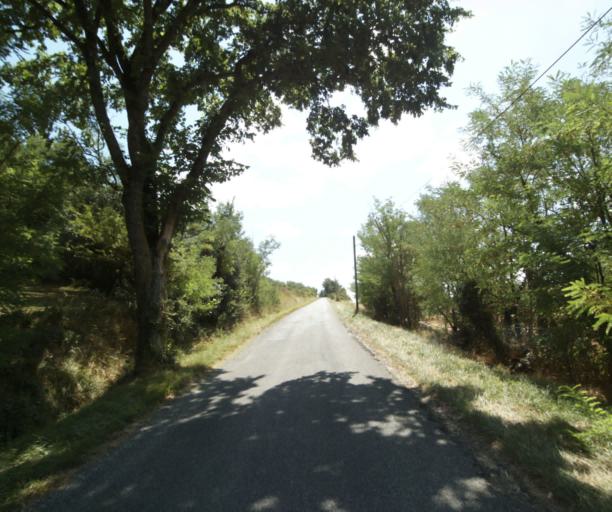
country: FR
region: Midi-Pyrenees
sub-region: Departement de la Haute-Garonne
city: Saint-Felix-Lauragais
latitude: 43.4688
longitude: 1.8502
